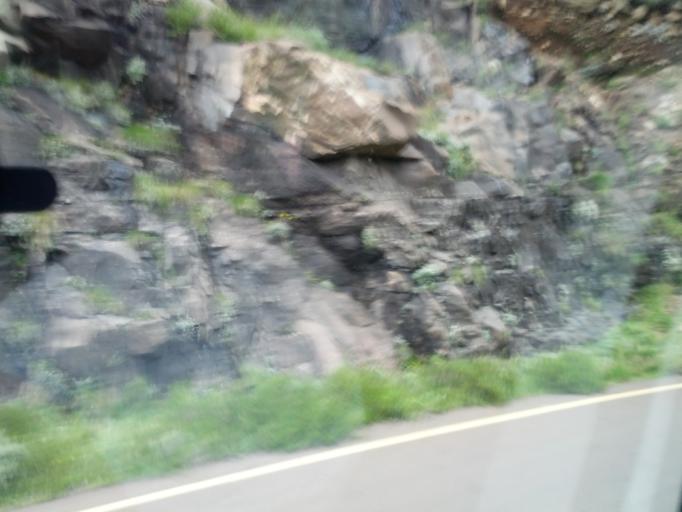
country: LS
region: Butha-Buthe
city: Butha-Buthe
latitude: -29.0652
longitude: 28.3704
